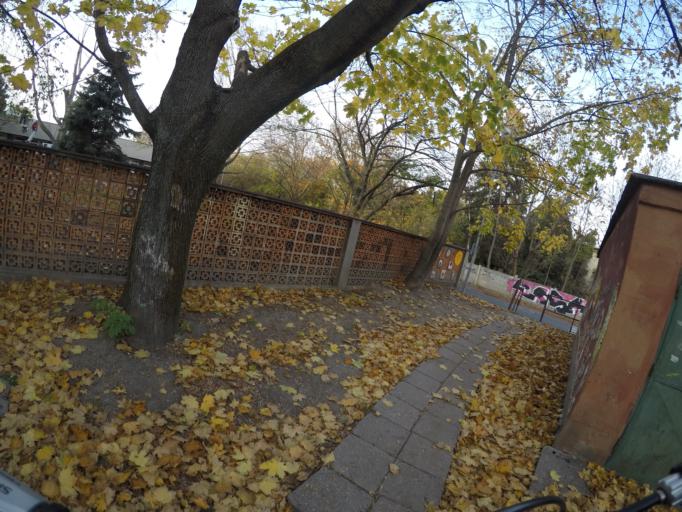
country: SK
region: Bratislavsky
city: Bratislava
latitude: 48.1750
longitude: 17.1601
